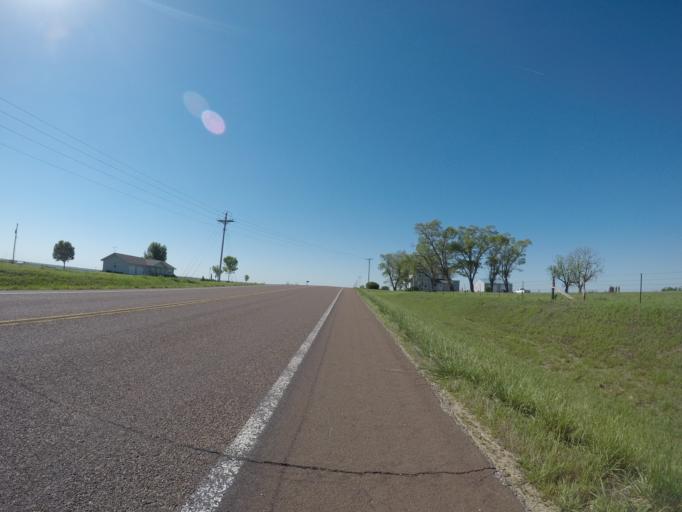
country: US
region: Kansas
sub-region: Osage County
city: Overbrook
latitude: 38.9282
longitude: -95.4562
